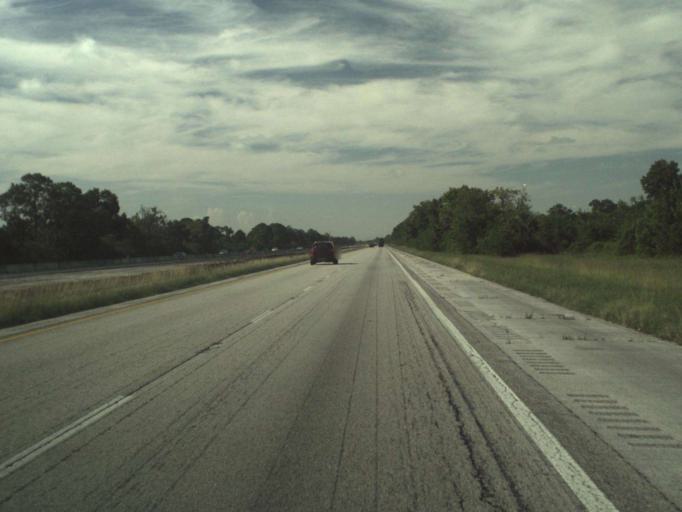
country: US
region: Florida
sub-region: Indian River County
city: Fellsmere
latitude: 27.7228
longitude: -80.5455
